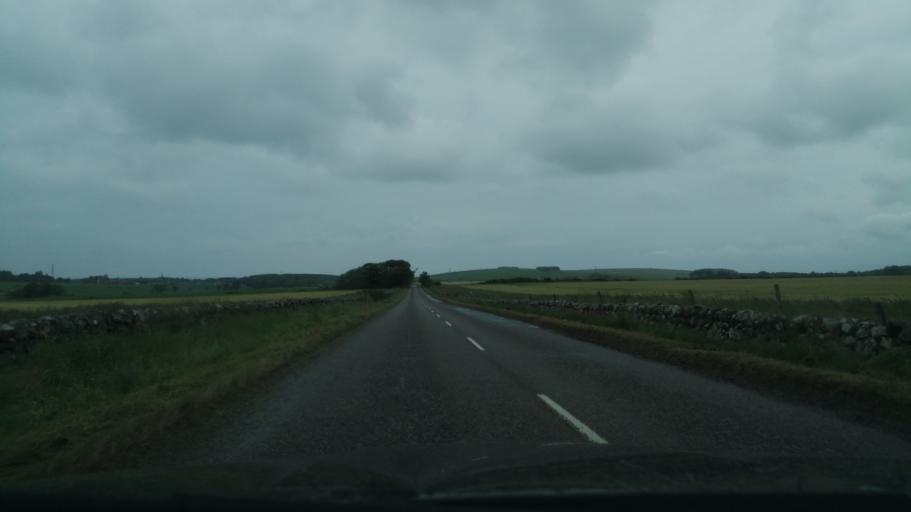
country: GB
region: Scotland
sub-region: Aberdeenshire
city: Portsoy
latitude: 57.6597
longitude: -2.6982
